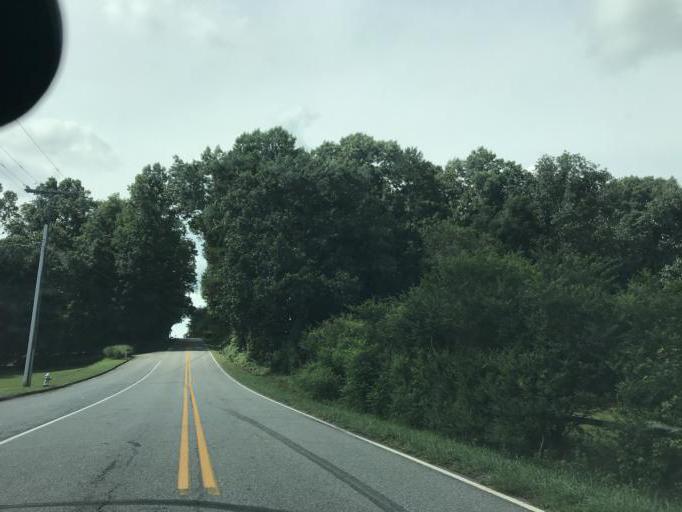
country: US
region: Georgia
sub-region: Forsyth County
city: Cumming
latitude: 34.2159
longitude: -84.2377
